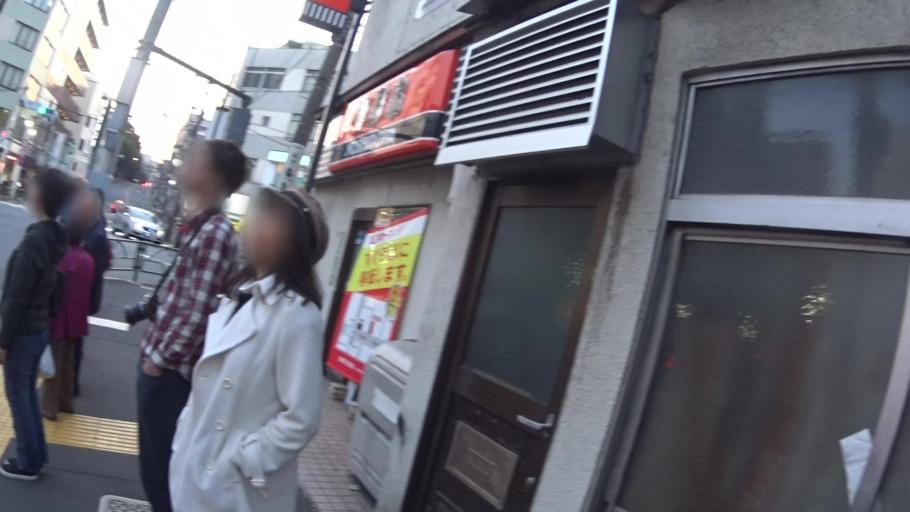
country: JP
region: Tokyo
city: Tokyo
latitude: 35.7181
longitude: 139.7654
